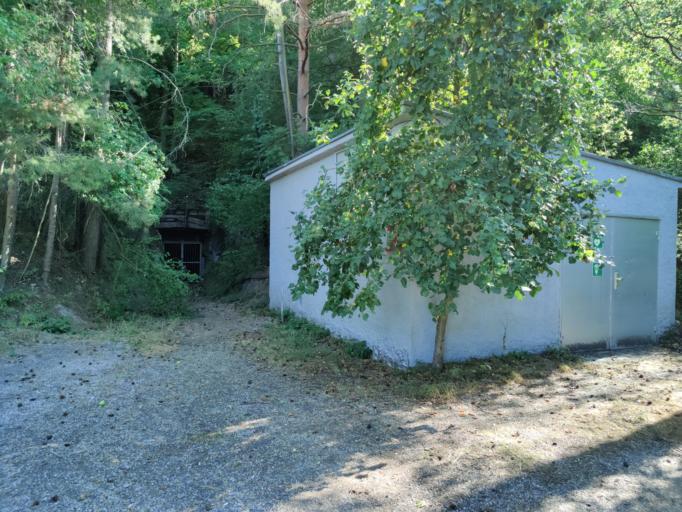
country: LU
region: Luxembourg
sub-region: Canton de Luxembourg
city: Walferdange
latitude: 49.6606
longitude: 6.1453
